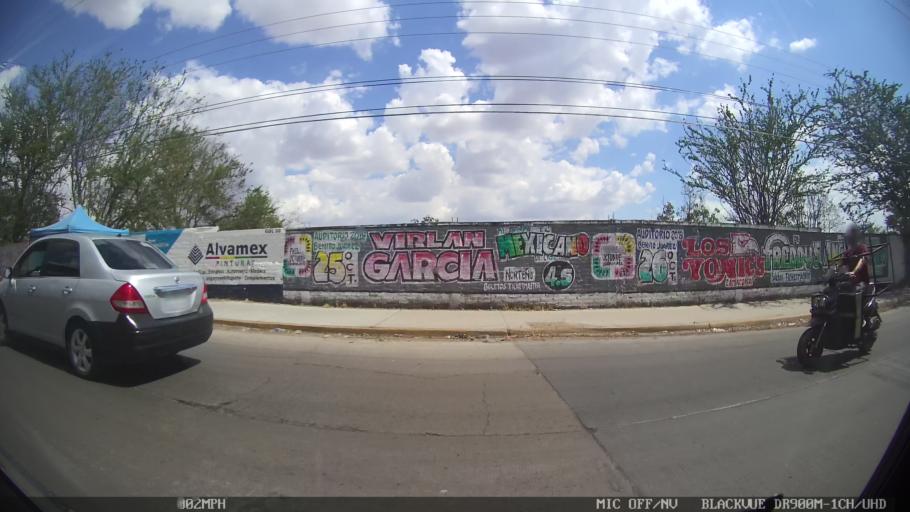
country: MX
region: Jalisco
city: Tlaquepaque
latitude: 20.6766
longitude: -103.2631
